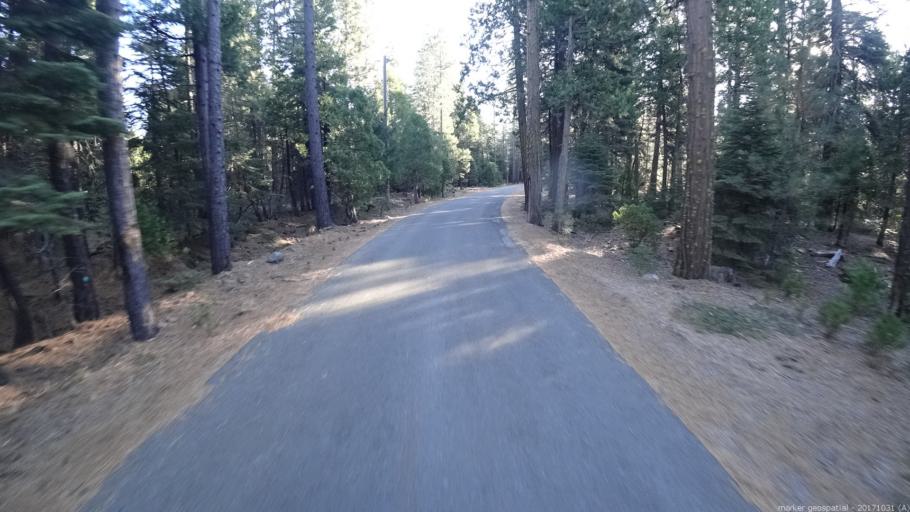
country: US
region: California
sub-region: Shasta County
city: Shingletown
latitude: 40.5246
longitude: -121.7869
